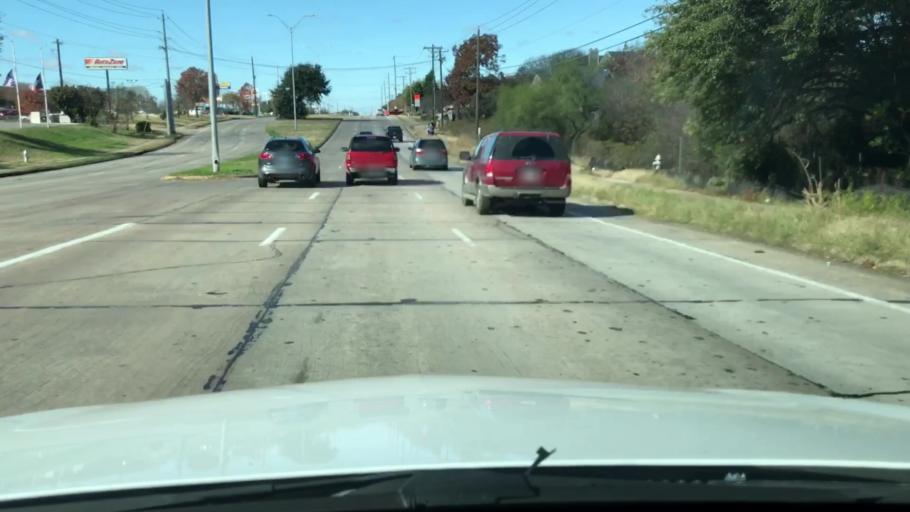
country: US
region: Texas
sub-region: Travis County
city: Onion Creek
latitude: 30.1877
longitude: -97.7626
